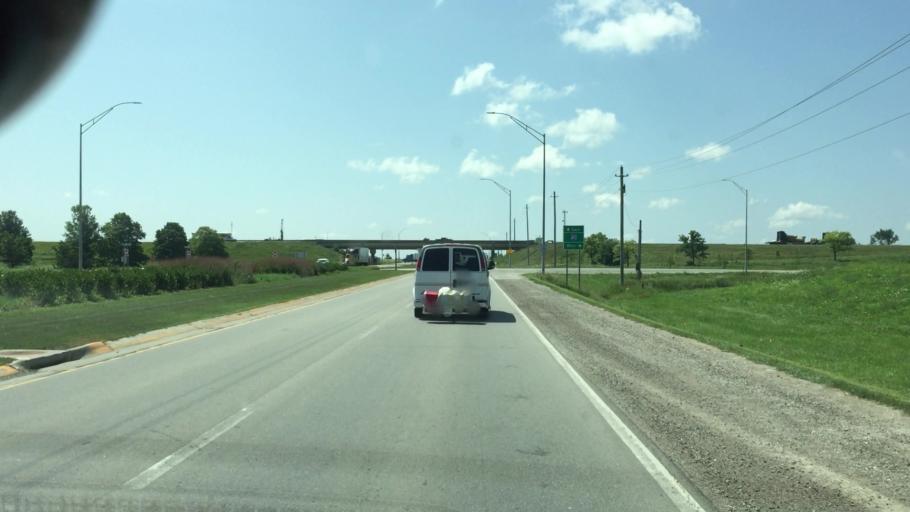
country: US
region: Iowa
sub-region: Poweshiek County
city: Grinnell
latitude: 41.6989
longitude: -92.7273
